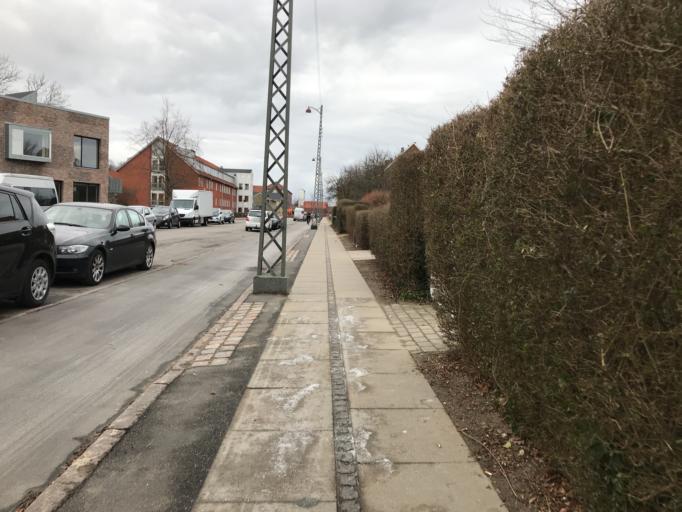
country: DK
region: Capital Region
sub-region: Kobenhavn
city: Vanlose
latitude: 55.6912
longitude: 12.4982
